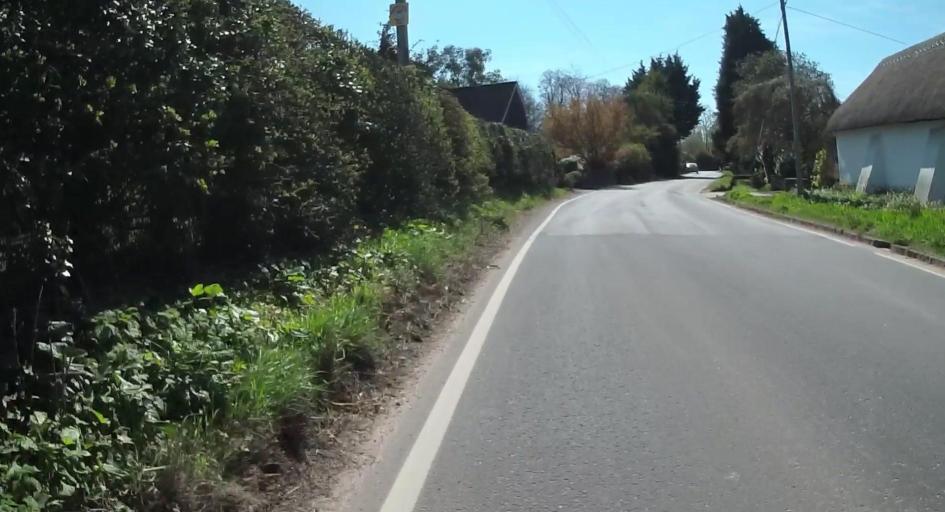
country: GB
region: England
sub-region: Hampshire
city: Romsey
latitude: 51.0797
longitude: -1.4777
